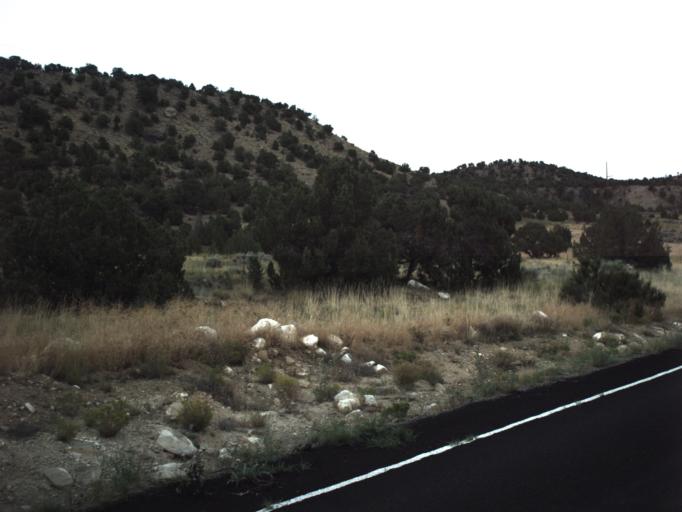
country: US
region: Utah
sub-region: Carbon County
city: East Carbon City
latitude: 39.4915
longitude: -110.4037
